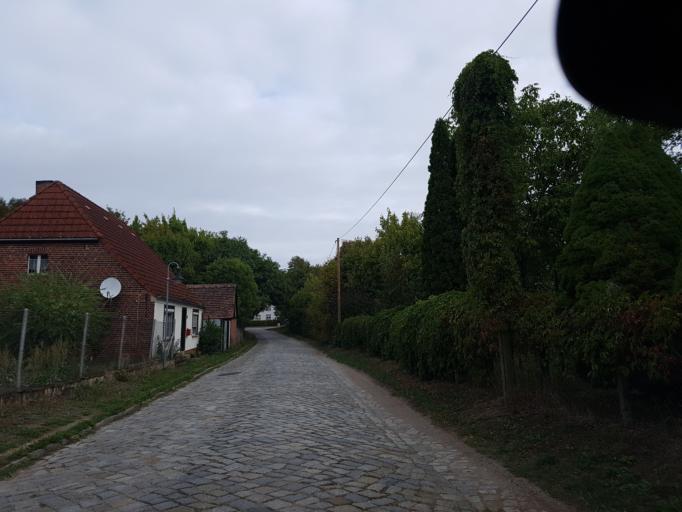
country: DE
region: Saxony-Anhalt
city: Lindau
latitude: 52.0274
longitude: 12.2252
